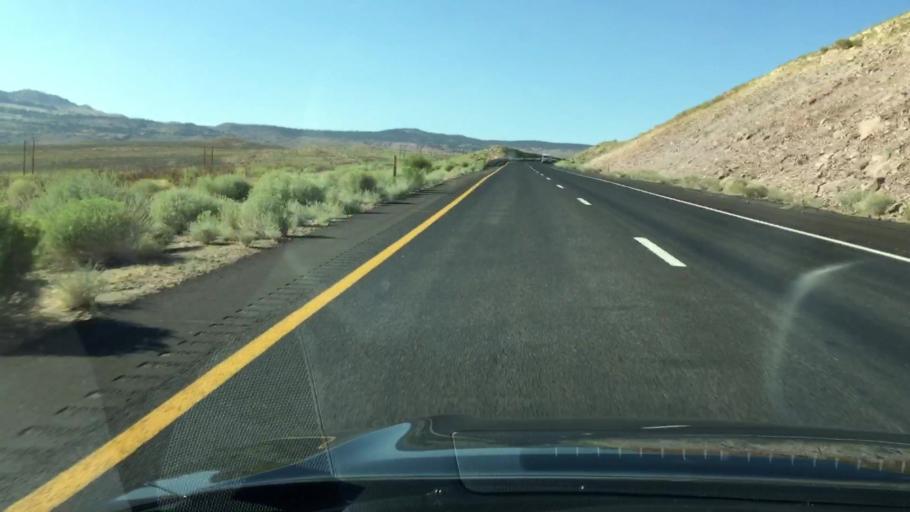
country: US
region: California
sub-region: Inyo County
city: West Bishop
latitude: 37.4695
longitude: -118.5794
